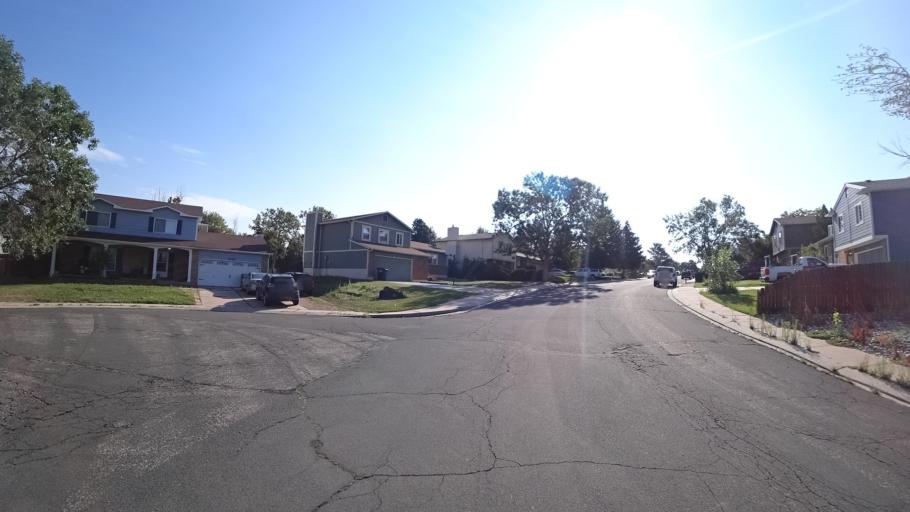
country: US
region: Colorado
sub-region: El Paso County
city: Air Force Academy
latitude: 38.9442
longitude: -104.7785
